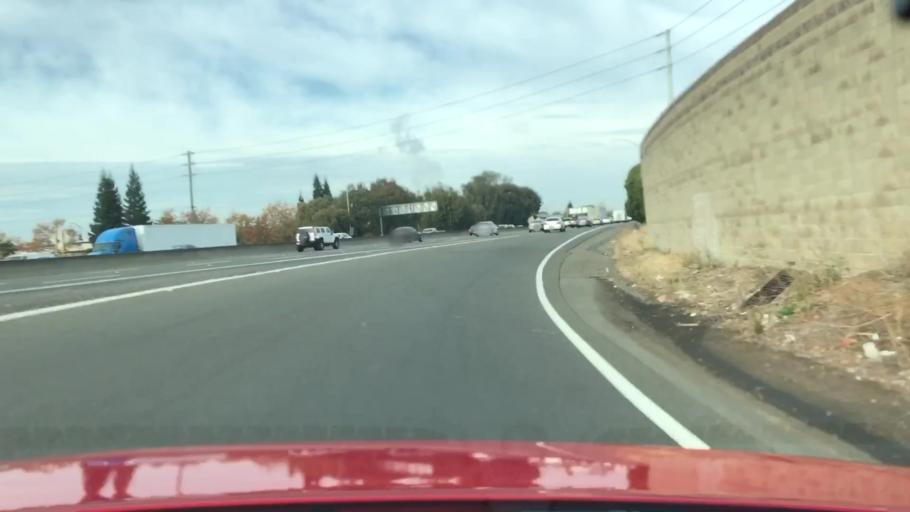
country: US
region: California
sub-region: Sacramento County
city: Parkway
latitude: 38.4976
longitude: -121.4471
